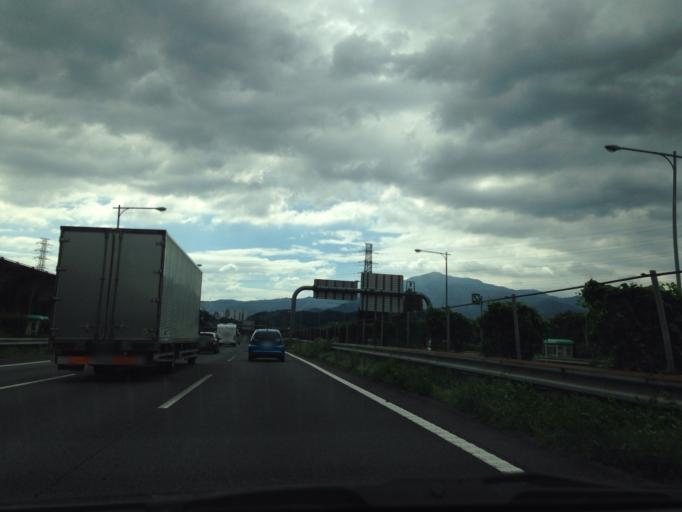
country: JP
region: Kanagawa
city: Atsugi
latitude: 35.4250
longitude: 139.3460
